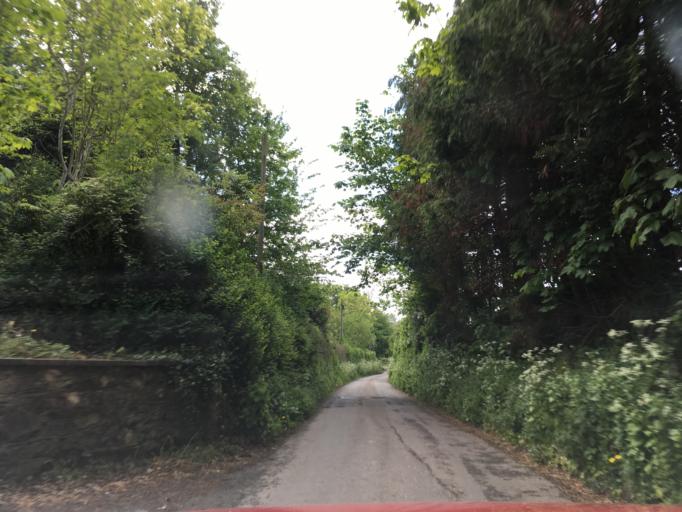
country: GB
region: England
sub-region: Gloucestershire
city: Dursley
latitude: 51.6868
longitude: -2.3931
